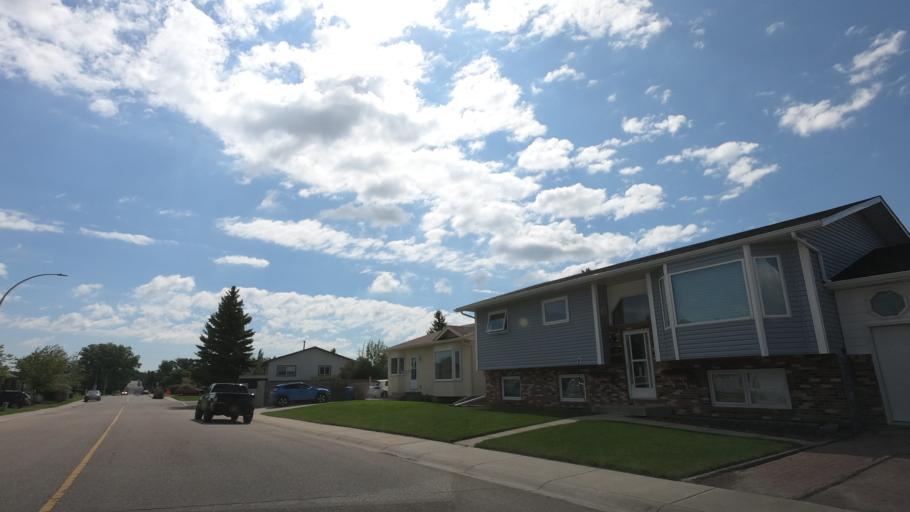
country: CA
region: Alberta
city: Airdrie
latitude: 51.2851
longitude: -114.0176
